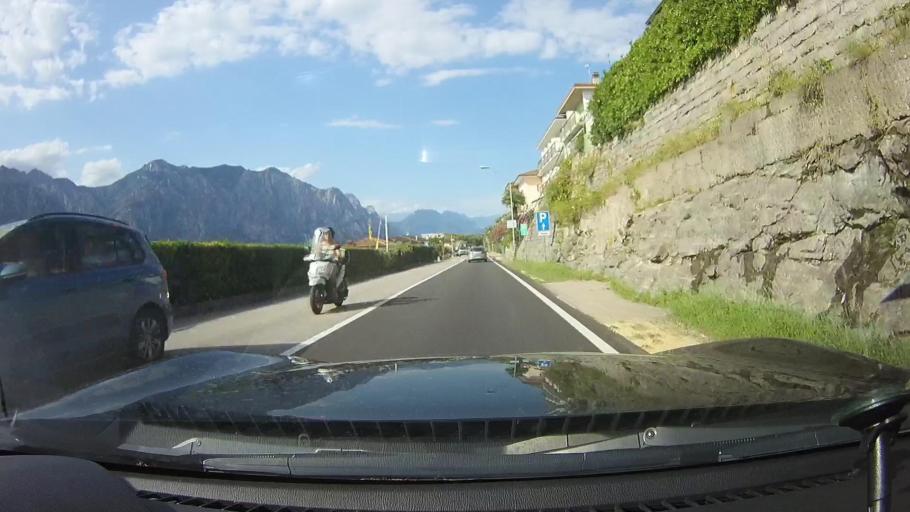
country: IT
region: Veneto
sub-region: Provincia di Verona
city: Malcesine
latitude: 45.7715
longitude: 10.8125
